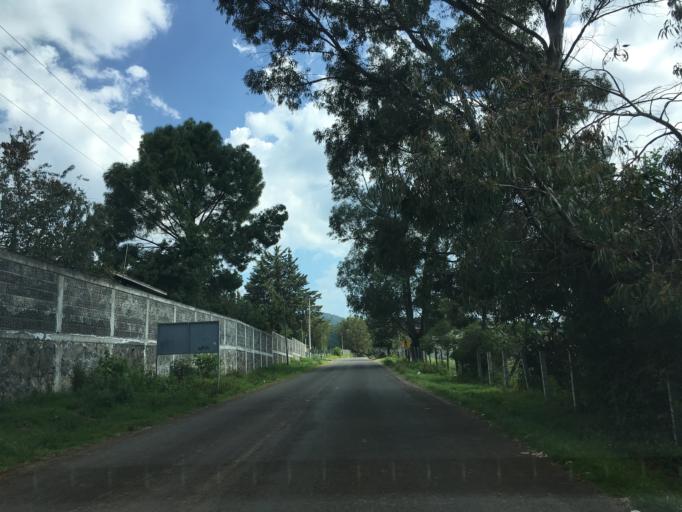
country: MX
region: Michoacan
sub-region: Morelia
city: Montana Monarca (Punta Altozano)
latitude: 19.5863
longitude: -101.1896
